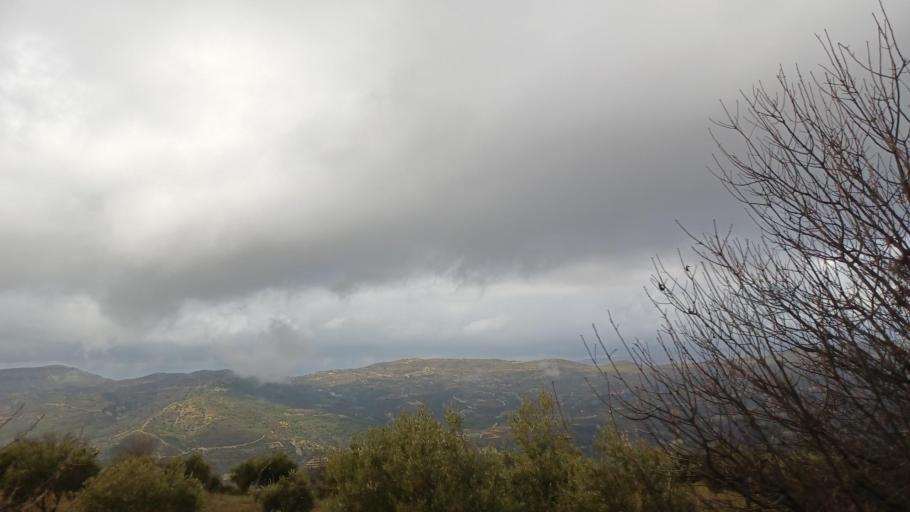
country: CY
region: Limassol
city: Pachna
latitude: 34.8346
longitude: 32.7444
